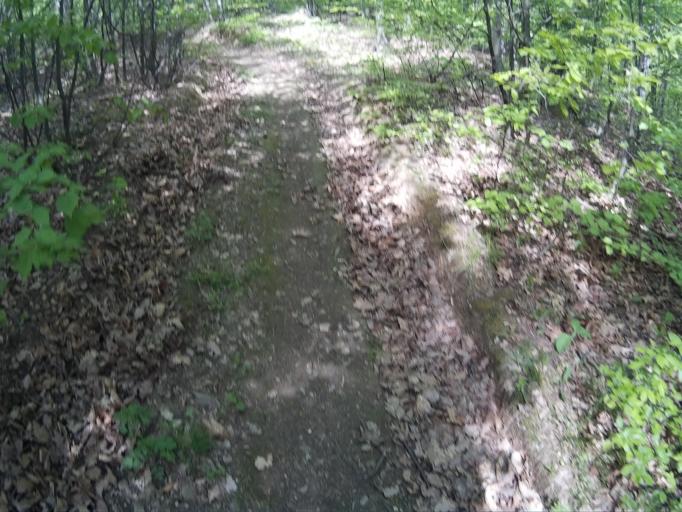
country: HU
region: Vas
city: Koszeg
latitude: 47.3557
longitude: 16.5048
